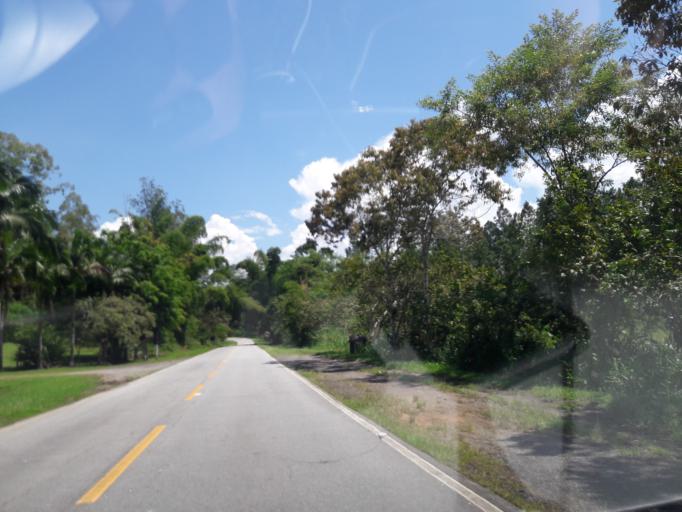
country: BR
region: Parana
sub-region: Antonina
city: Antonina
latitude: -25.5241
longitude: -48.7834
